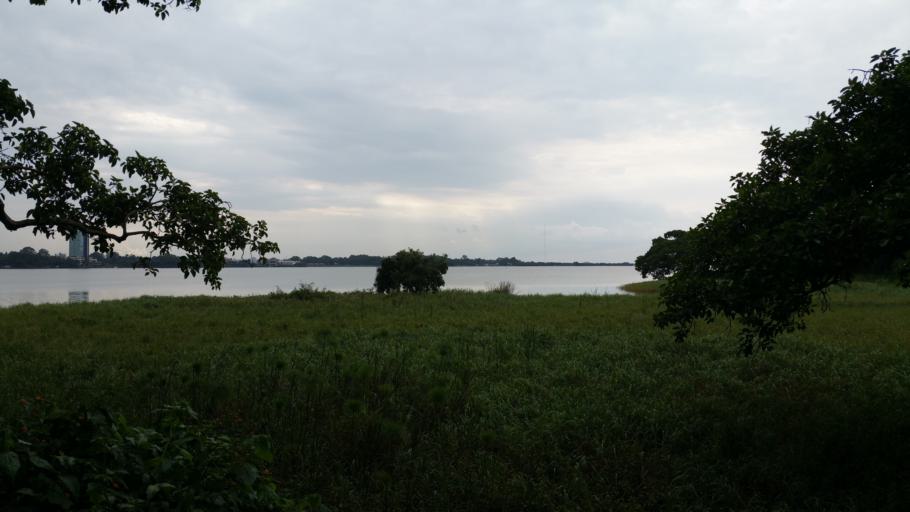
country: ET
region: Amhara
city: Bahir Dar
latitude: 11.6014
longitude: 37.3957
